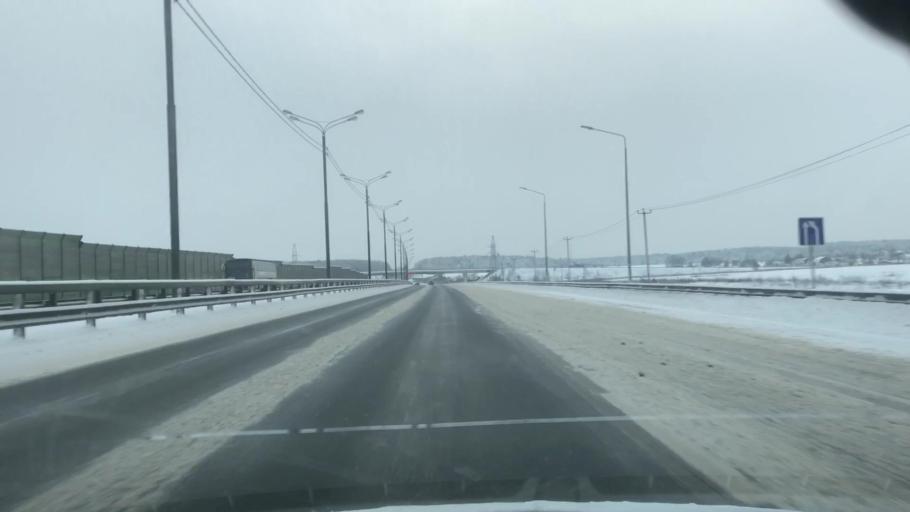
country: RU
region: Moskovskaya
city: Mikhnevo
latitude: 55.1905
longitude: 37.8958
